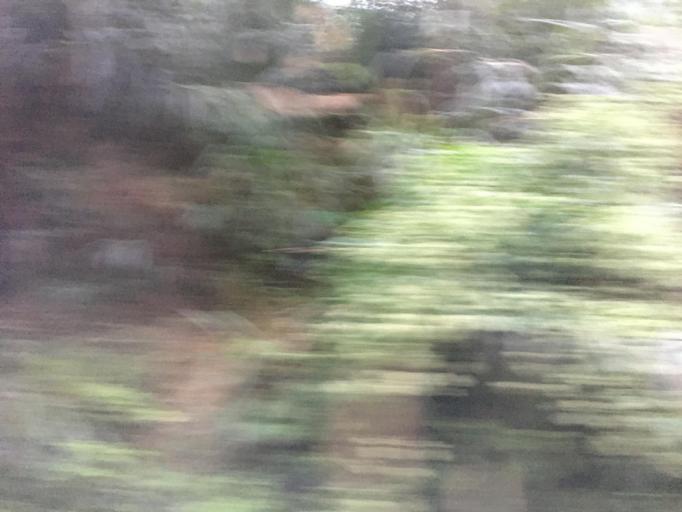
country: TW
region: Taiwan
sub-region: Chiayi
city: Jiayi Shi
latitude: 23.5267
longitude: 120.6527
